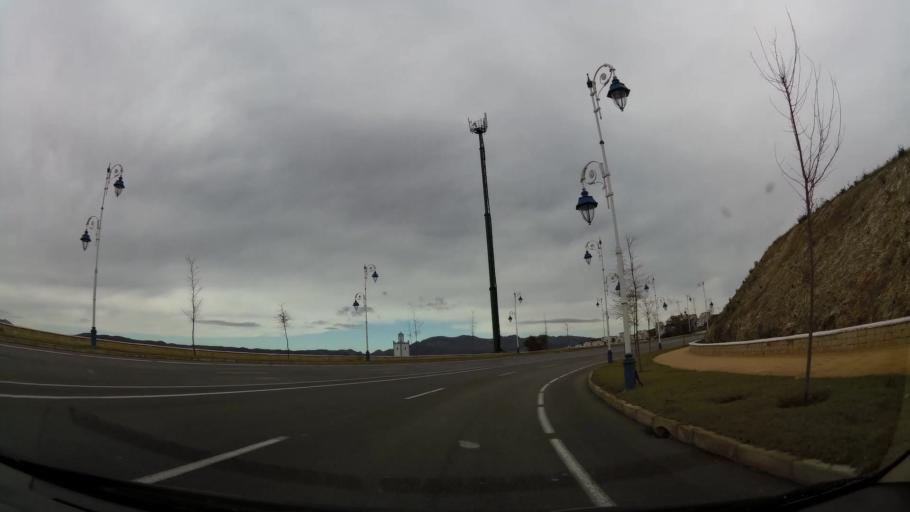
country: MA
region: Tanger-Tetouan
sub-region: Tetouan
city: Martil
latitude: 35.6649
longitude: -5.2973
